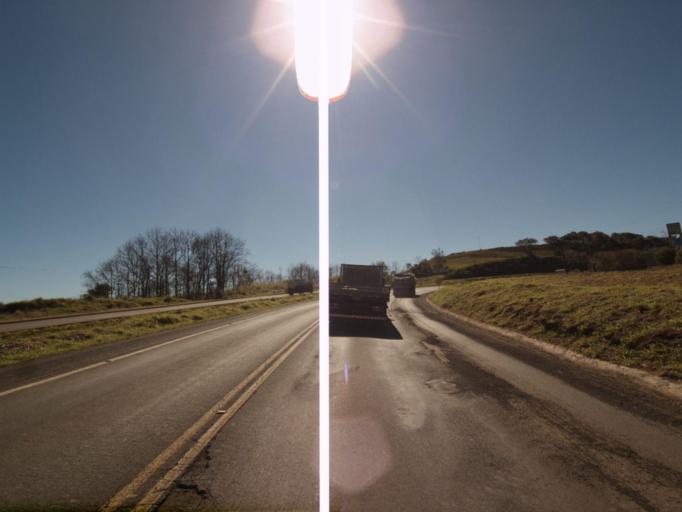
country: BR
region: Santa Catarina
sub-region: Chapeco
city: Chapeco
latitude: -26.8282
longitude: -53.0095
